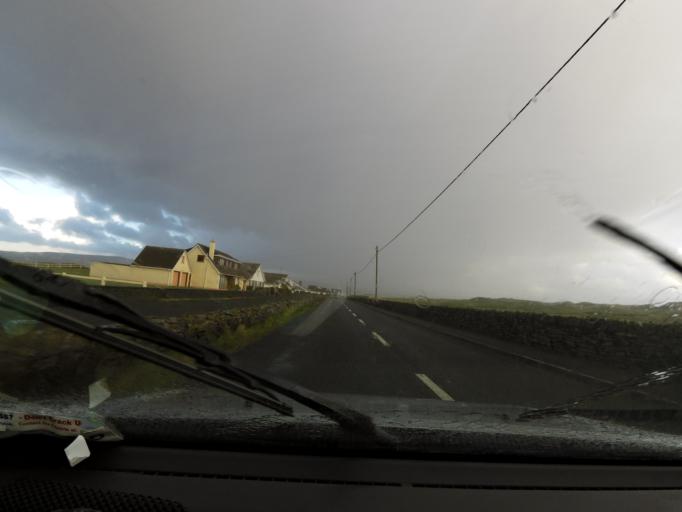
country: IE
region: Munster
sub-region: An Clar
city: Kilrush
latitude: 52.9421
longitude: -9.3491
